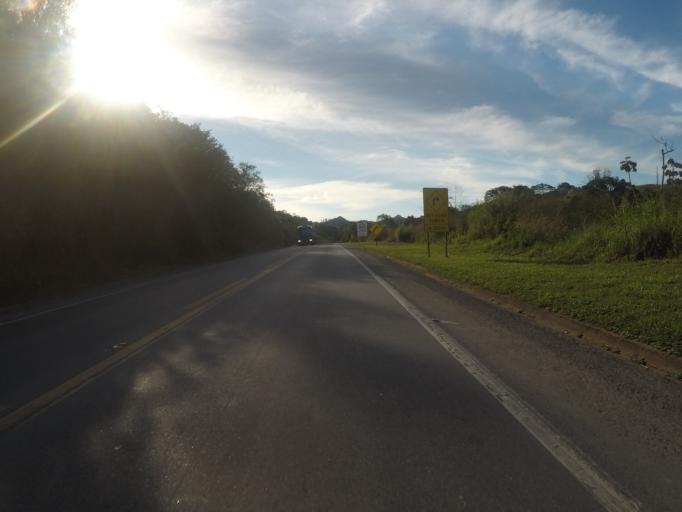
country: BR
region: Espirito Santo
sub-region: Fundao
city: Fundao
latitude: -19.8825
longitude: -40.4163
